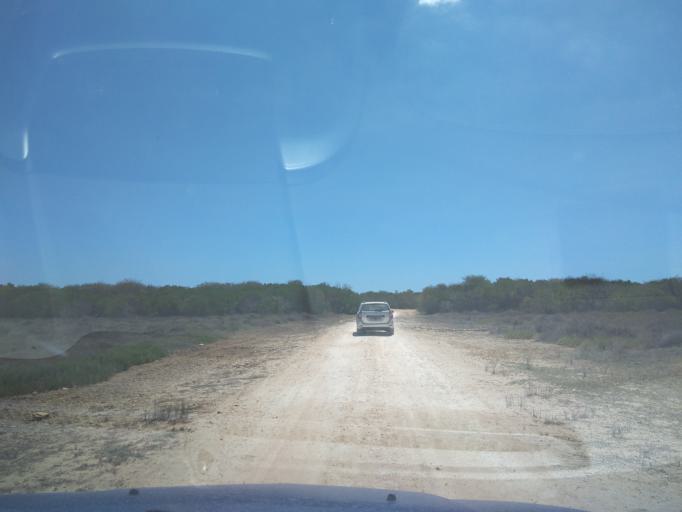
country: TN
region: Susah
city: Harqalah
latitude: 36.1624
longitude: 10.4624
